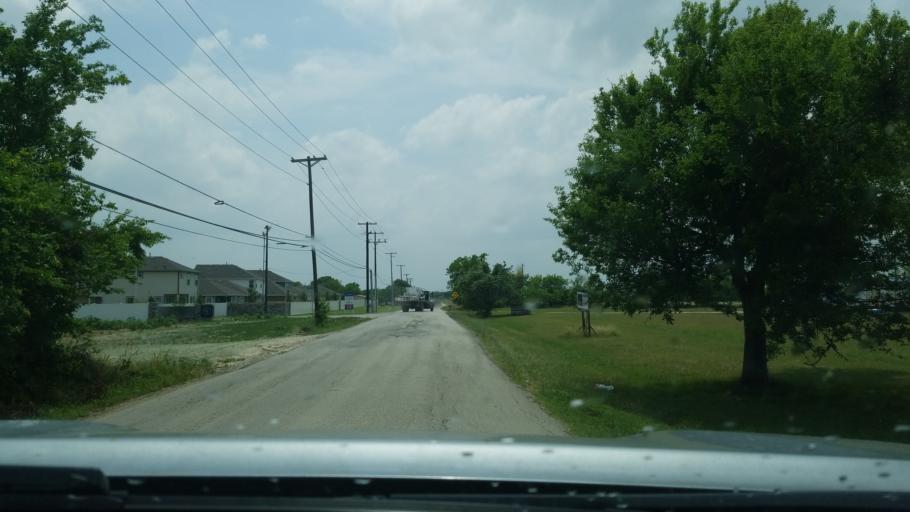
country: US
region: Texas
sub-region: Comal County
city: New Braunfels
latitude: 29.7441
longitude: -98.0799
